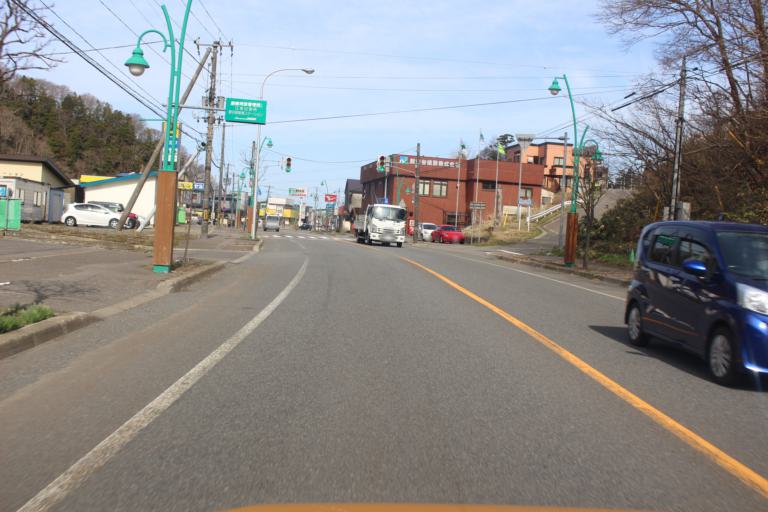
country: JP
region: Hokkaido
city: Kamiiso
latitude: 41.9149
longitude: 140.2272
